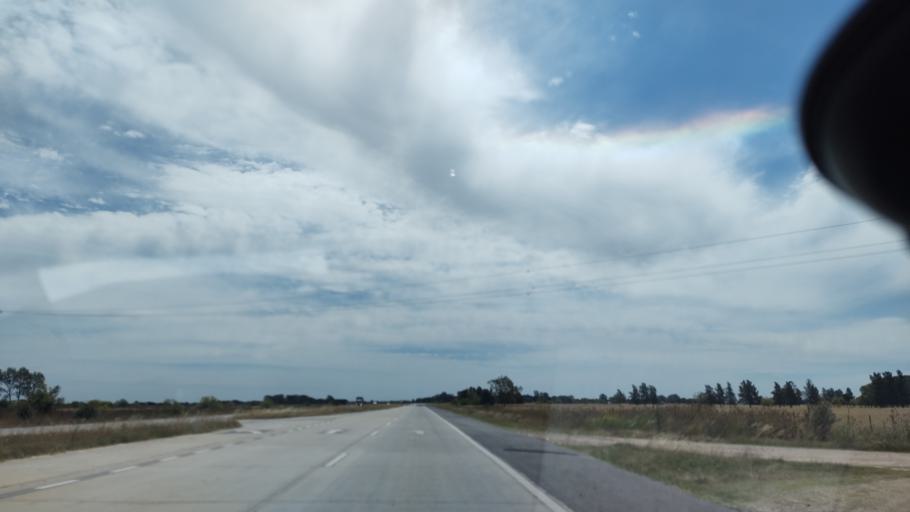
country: AR
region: Buenos Aires
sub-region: Partido de Brandsen
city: Brandsen
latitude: -35.0441
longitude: -58.1641
